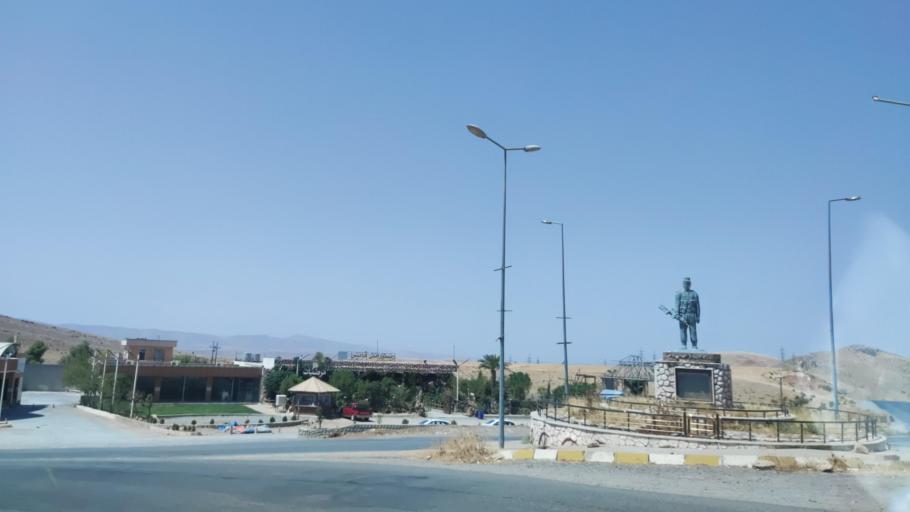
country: IQ
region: Arbil
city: Shaqlawah
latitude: 36.6083
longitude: 44.3093
